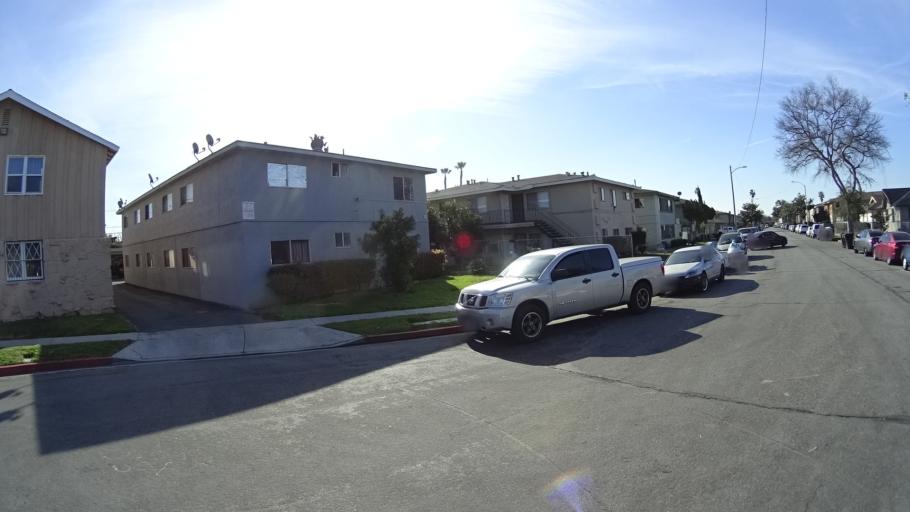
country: US
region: California
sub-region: Orange County
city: Fullerton
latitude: 33.8499
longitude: -117.9298
